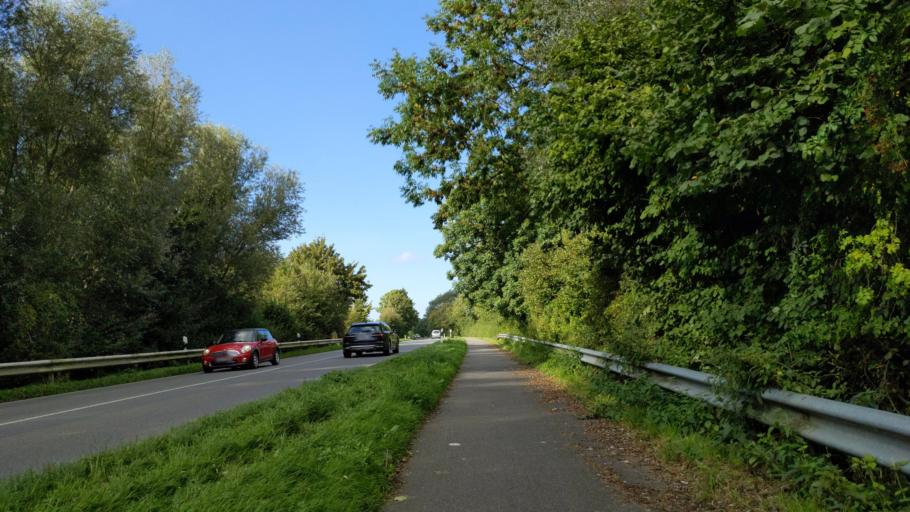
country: DE
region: Schleswig-Holstein
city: Stockelsdorf
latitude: 53.9344
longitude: 10.6336
